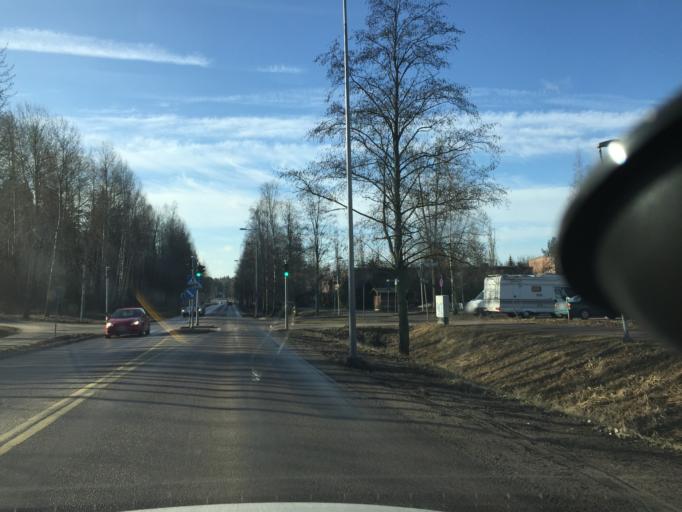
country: FI
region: Uusimaa
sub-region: Helsinki
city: Teekkarikylae
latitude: 60.2830
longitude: 24.8727
